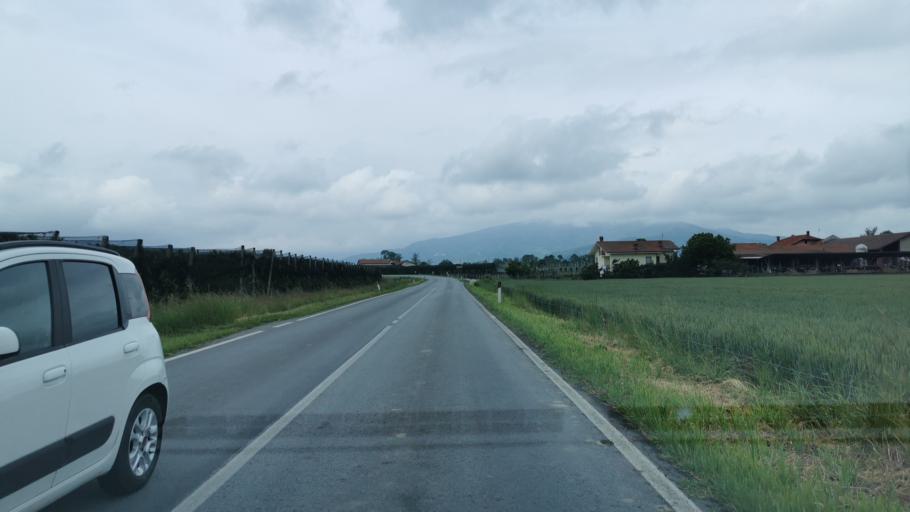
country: IT
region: Piedmont
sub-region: Provincia di Cuneo
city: Villafalletto
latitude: 44.5856
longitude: 7.5369
